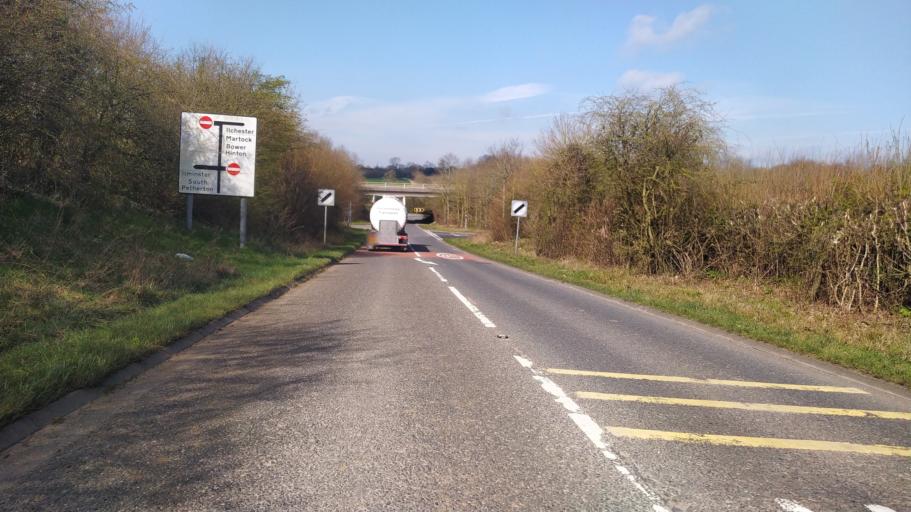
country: GB
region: England
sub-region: Somerset
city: Stoke-sub-Hamdon
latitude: 50.9491
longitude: -2.7721
